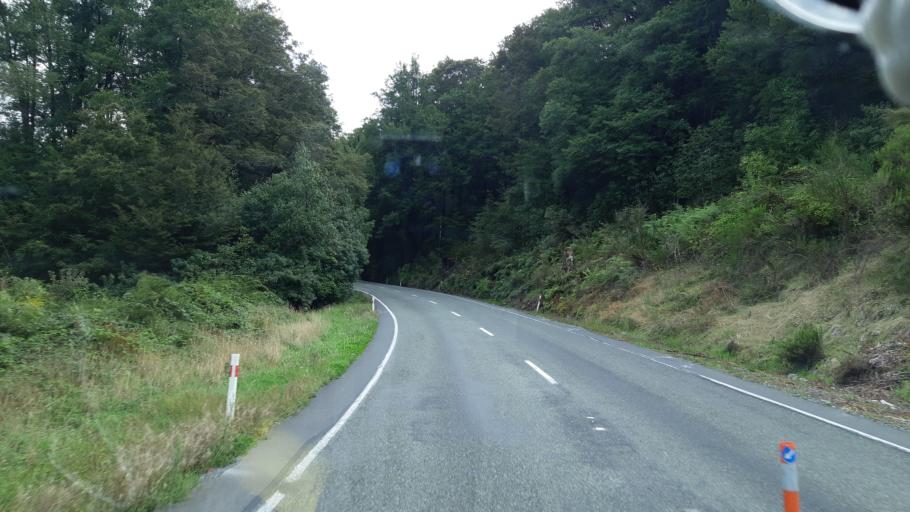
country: NZ
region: West Coast
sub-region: Buller District
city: Westport
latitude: -41.9575
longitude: 172.2003
